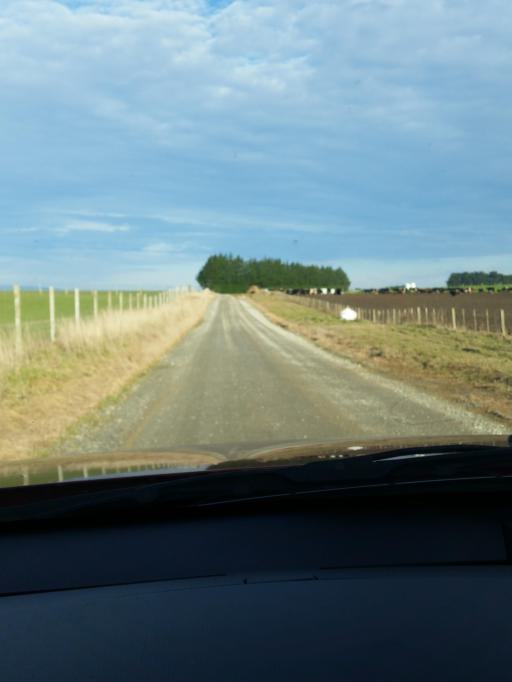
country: NZ
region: Southland
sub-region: Gore District
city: Gore
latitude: -46.2070
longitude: 168.7813
